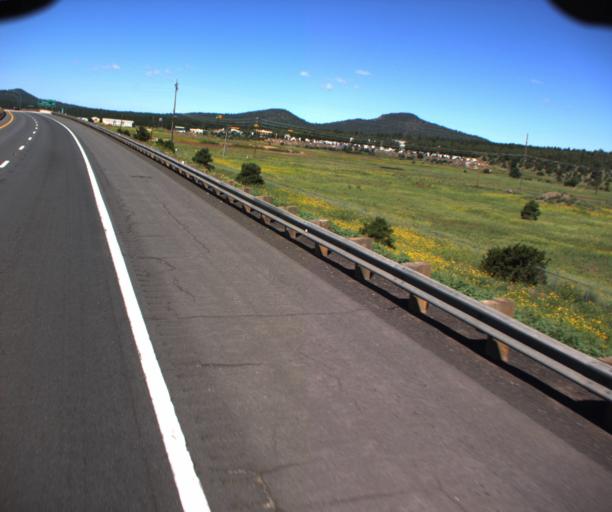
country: US
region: Arizona
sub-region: Coconino County
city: Williams
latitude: 35.2633
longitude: -112.1842
